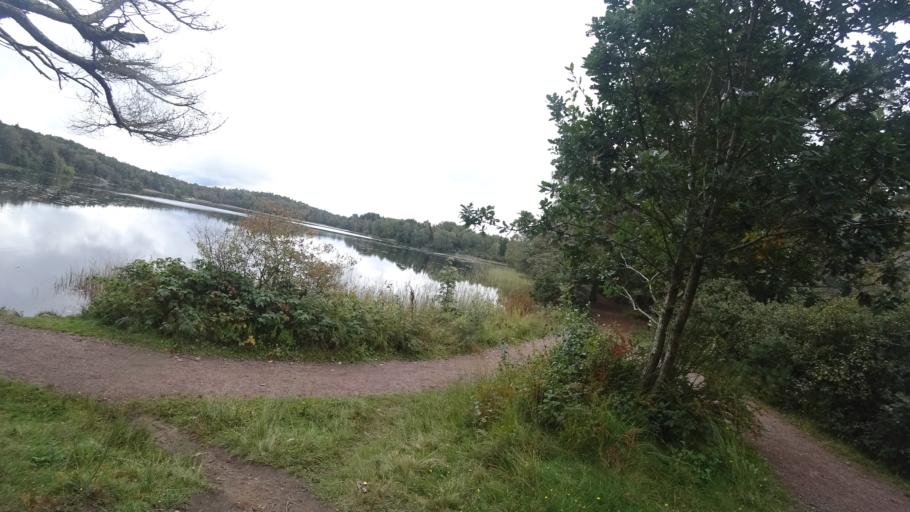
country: SE
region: Vaestra Goetaland
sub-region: Goteborg
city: Billdal
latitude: 57.6082
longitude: 11.9705
